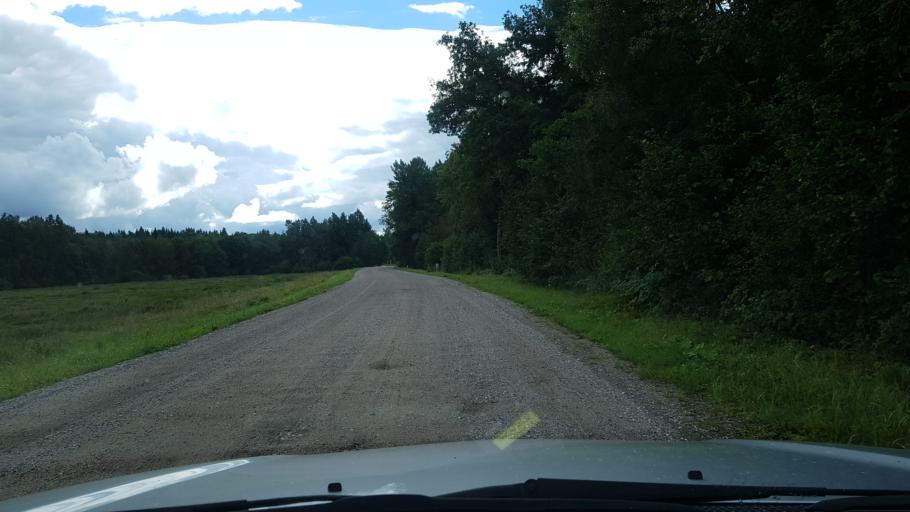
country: EE
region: Harju
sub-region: Rae vald
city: Vaida
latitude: 59.2645
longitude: 25.0489
